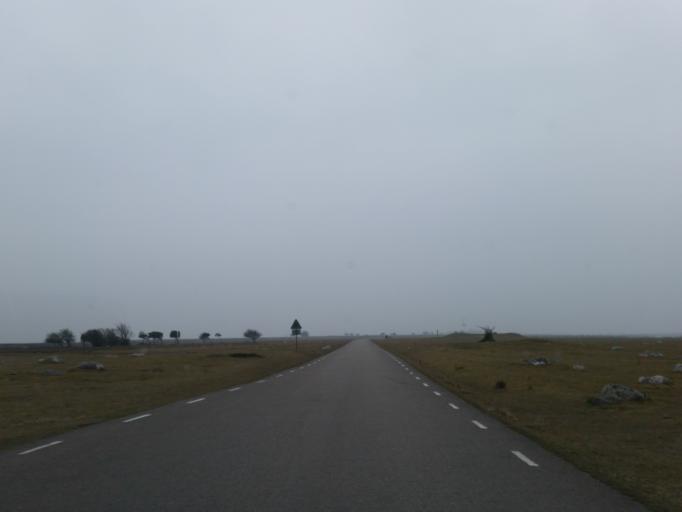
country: SE
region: Kalmar
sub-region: Morbylanga Kommun
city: Moerbylanga
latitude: 56.2119
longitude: 16.4070
